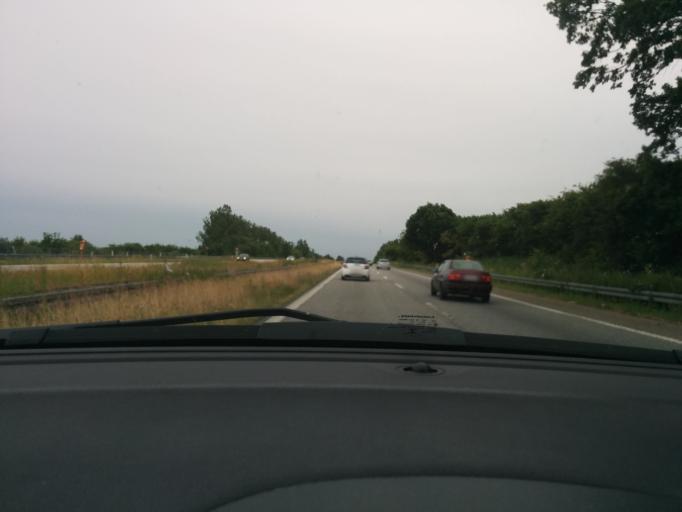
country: DK
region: Zealand
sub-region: Faxe Kommune
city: Ronnede
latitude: 55.3117
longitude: 12.0299
